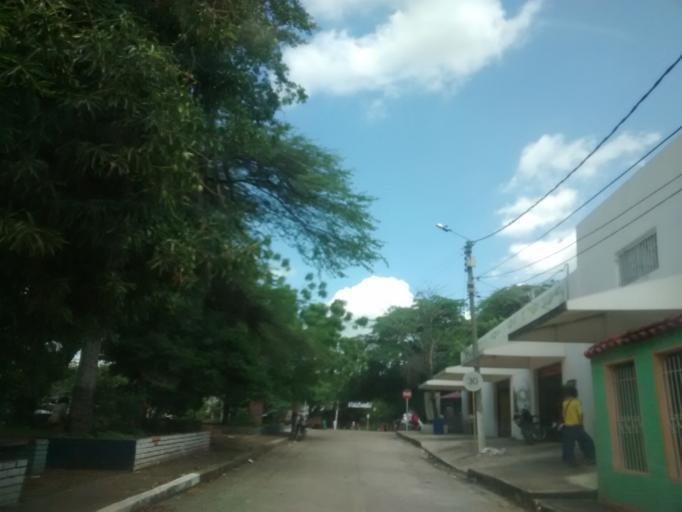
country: CO
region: Cundinamarca
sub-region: Girardot
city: Girardot City
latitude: 4.3100
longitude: -74.7909
